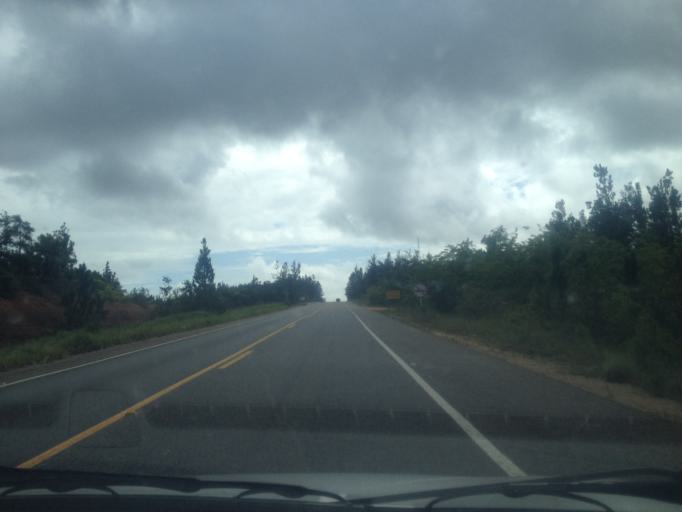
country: BR
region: Bahia
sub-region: Entre Rios
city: Entre Rios
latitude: -12.1372
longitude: -37.7915
